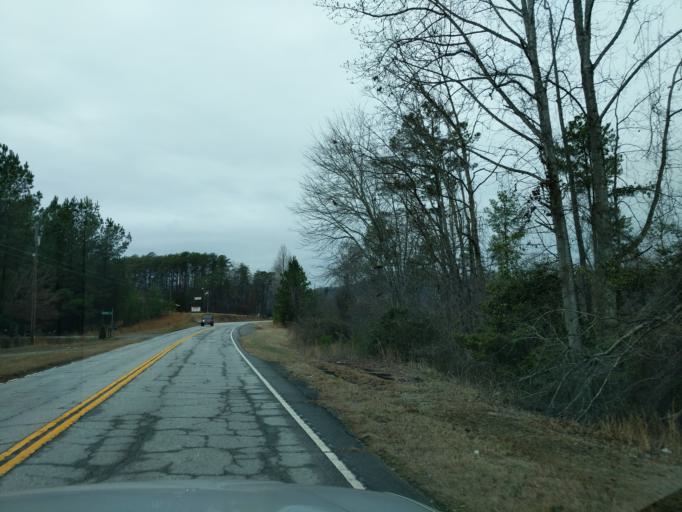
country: US
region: South Carolina
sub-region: Oconee County
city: Walhalla
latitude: 34.7859
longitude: -83.1131
